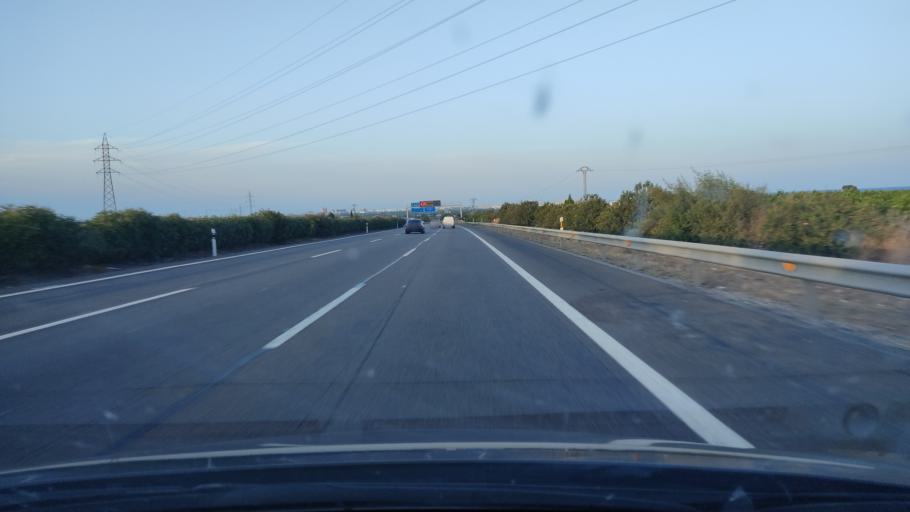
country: ES
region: Valencia
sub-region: Provincia de Valencia
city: Pucol
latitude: 39.6262
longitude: -0.3169
